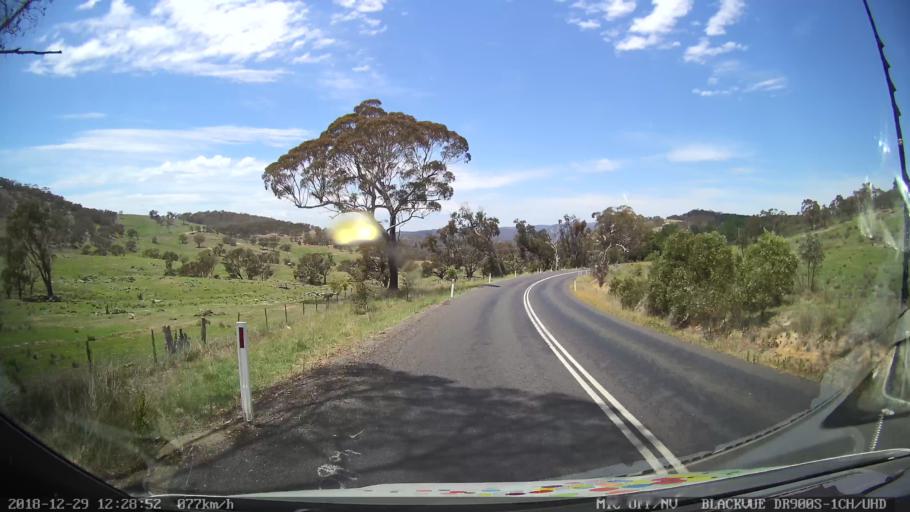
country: AU
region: Australian Capital Territory
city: Macarthur
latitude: -35.4912
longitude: 149.2280
